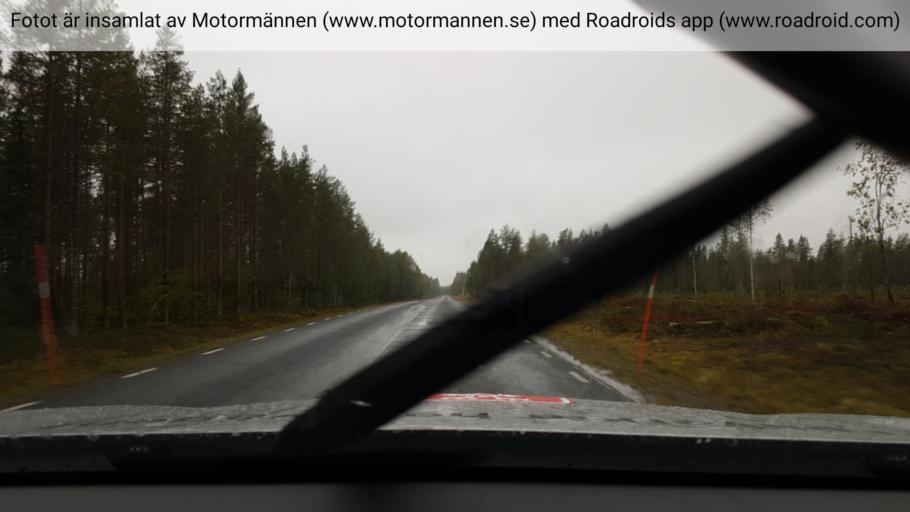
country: SE
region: Vaesterbotten
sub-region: Skelleftea Kommun
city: Storvik
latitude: 64.9659
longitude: 20.6639
